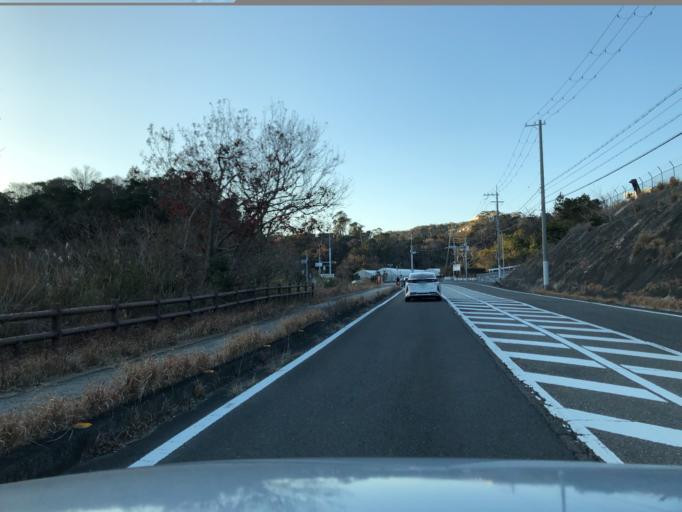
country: JP
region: Wakayama
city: Tanabe
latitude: 33.6623
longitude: 135.3746
